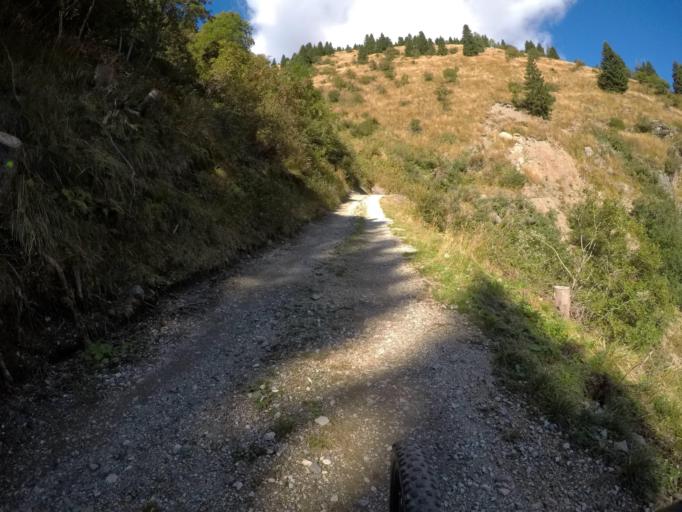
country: IT
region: Friuli Venezia Giulia
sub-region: Provincia di Udine
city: Ligosullo
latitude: 46.5564
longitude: 13.0901
